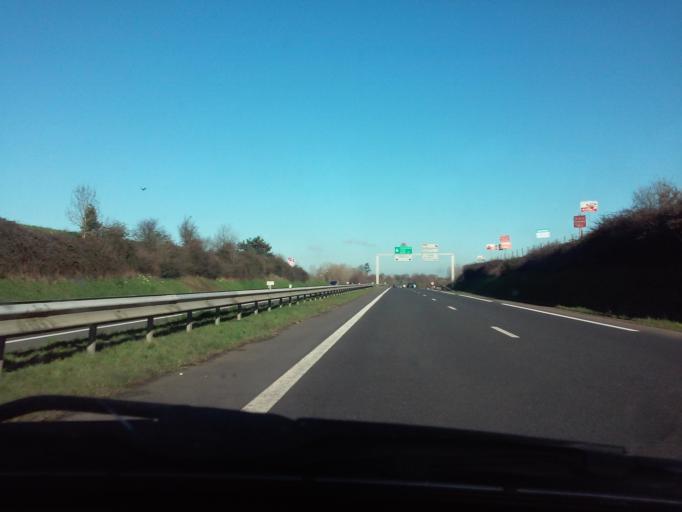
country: FR
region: Lower Normandy
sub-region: Departement de la Manche
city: Saint-Martin-des-Champs
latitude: 48.6464
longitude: -1.3466
